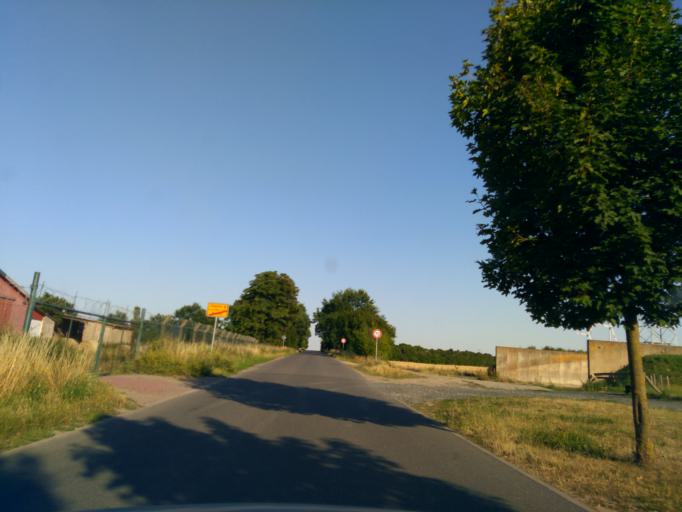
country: DE
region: Brandenburg
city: Wustermark
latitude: 52.5864
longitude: 12.9315
